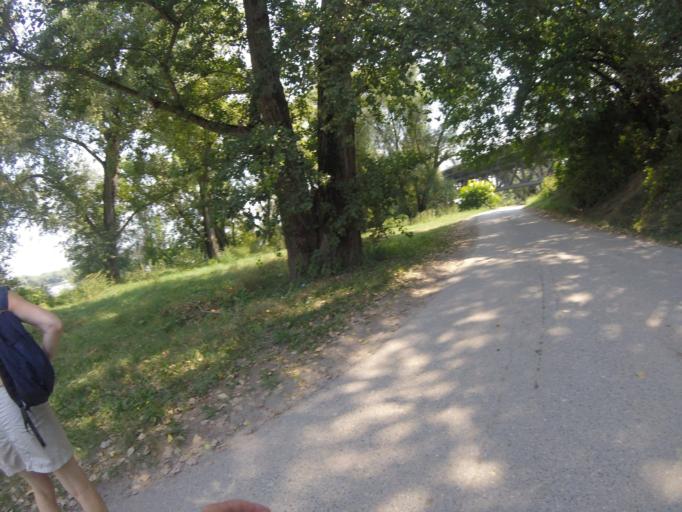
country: HU
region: Bacs-Kiskun
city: Baja
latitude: 46.1935
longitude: 18.9229
